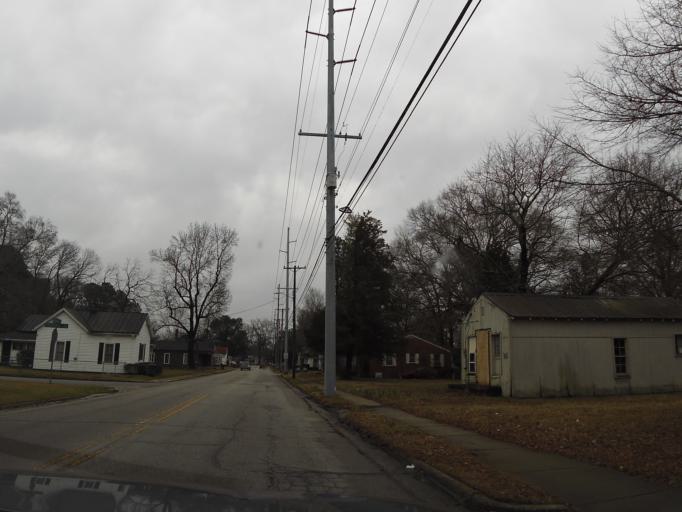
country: US
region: North Carolina
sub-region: Nash County
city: Rocky Mount
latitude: 35.9280
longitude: -77.8144
